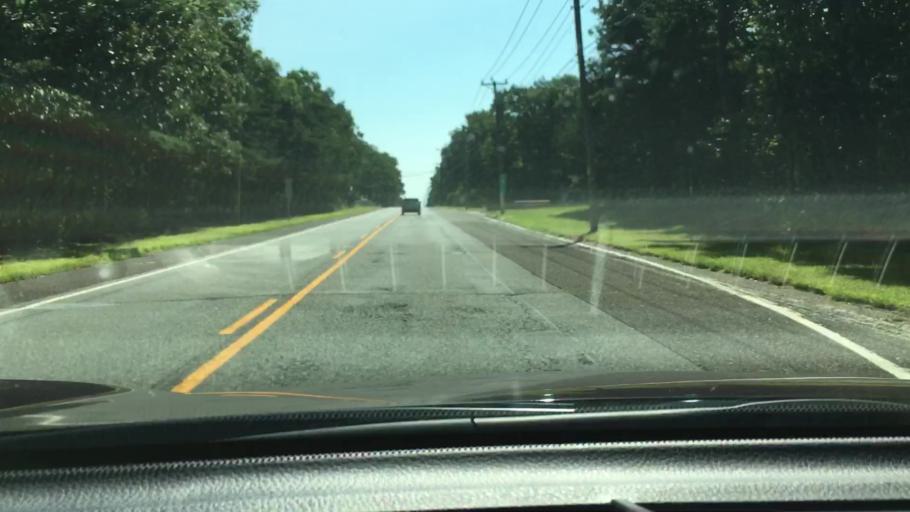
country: US
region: New Jersey
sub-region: Cumberland County
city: Millville
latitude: 39.3820
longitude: -74.9742
